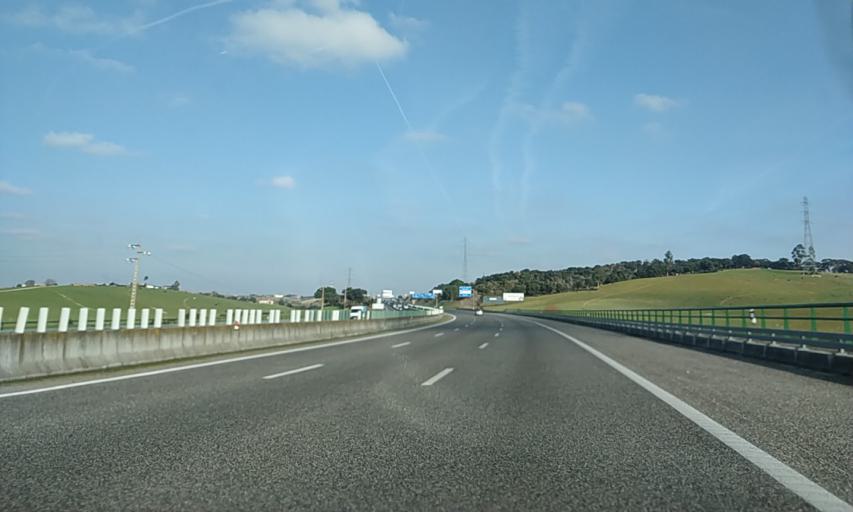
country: PT
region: Santarem
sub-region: Santarem
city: Santarem
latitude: 39.2440
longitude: -8.7430
